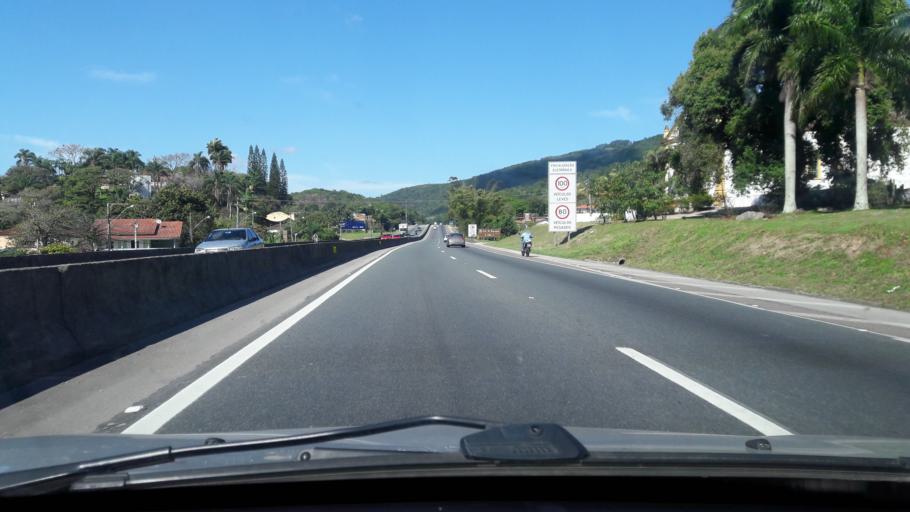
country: BR
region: Santa Catarina
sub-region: Biguacu
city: Biguacu
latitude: -27.4565
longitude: -48.6370
